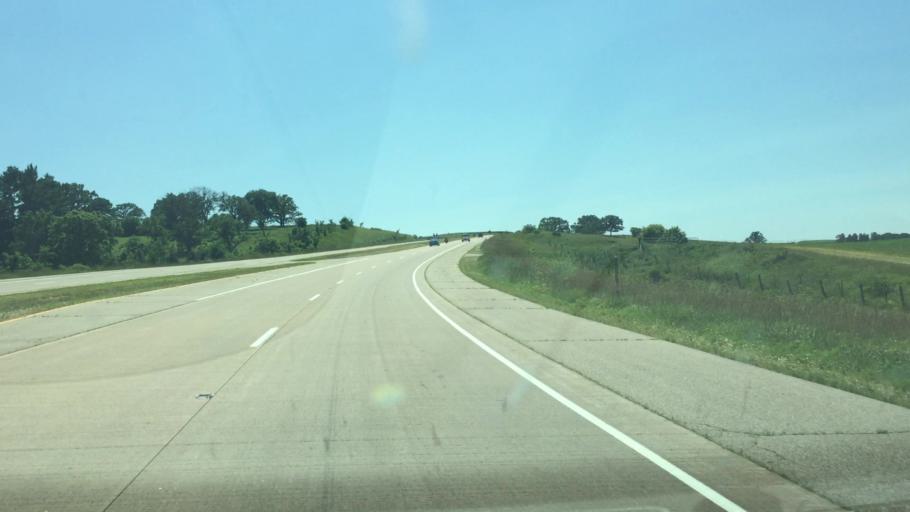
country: US
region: Wisconsin
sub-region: Iowa County
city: Mineral Point
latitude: 42.8099
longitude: -90.2614
